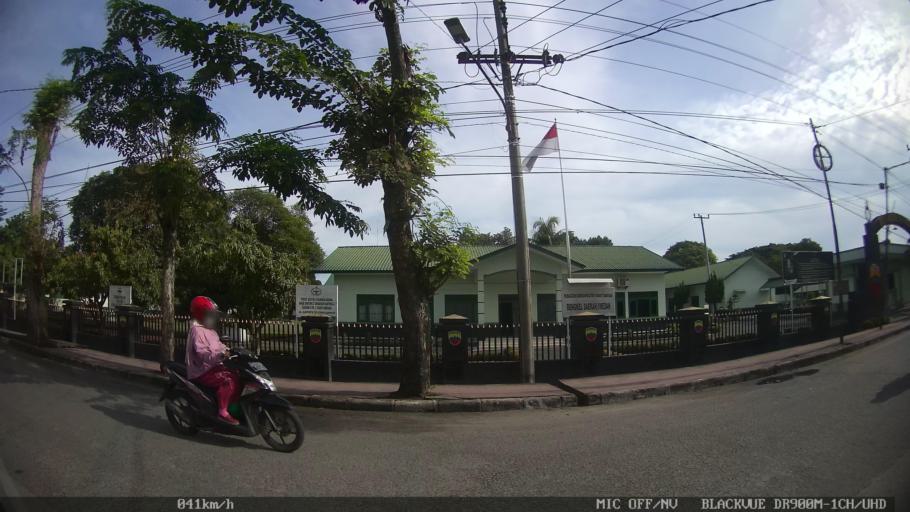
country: ID
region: North Sumatra
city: Sunggal
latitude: 3.6051
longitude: 98.6336
